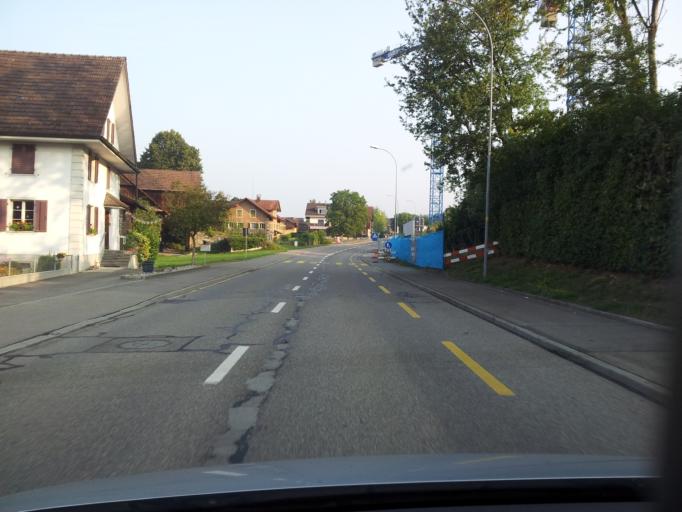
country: CH
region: Lucerne
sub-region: Sursee District
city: Schenkon
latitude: 47.1702
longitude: 8.1402
